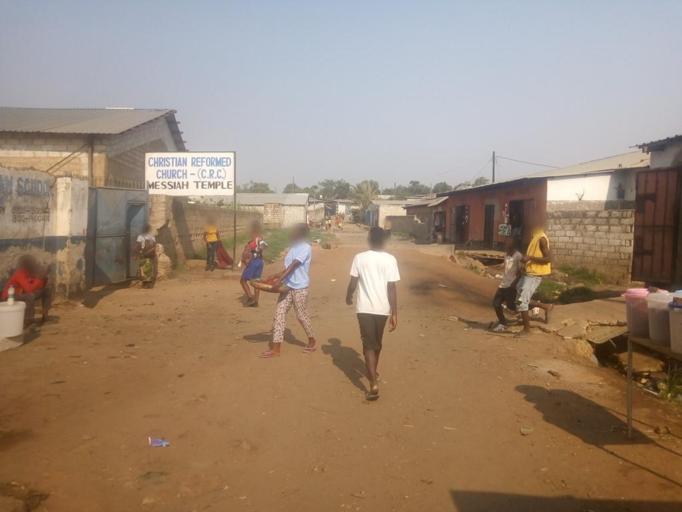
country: ZM
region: Lusaka
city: Lusaka
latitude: -15.4074
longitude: 28.3613
